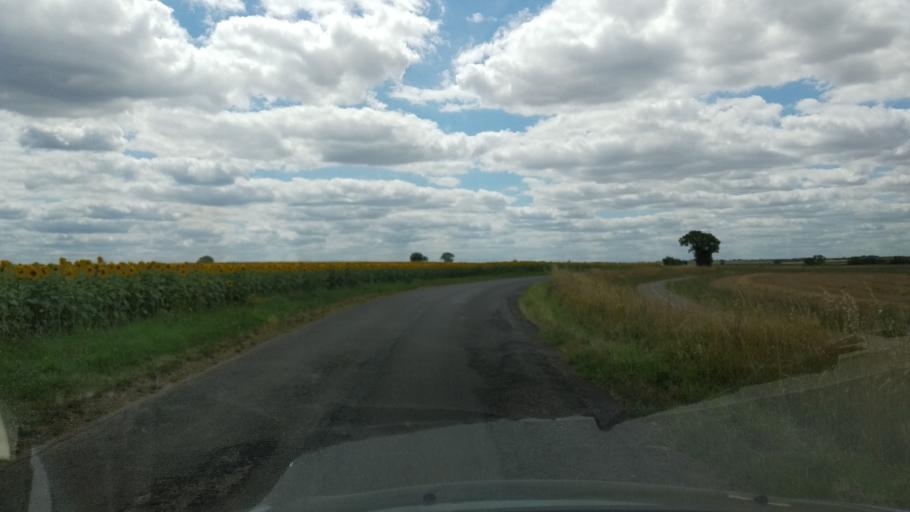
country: FR
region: Poitou-Charentes
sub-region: Departement de la Vienne
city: Avanton
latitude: 46.6741
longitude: 0.3364
